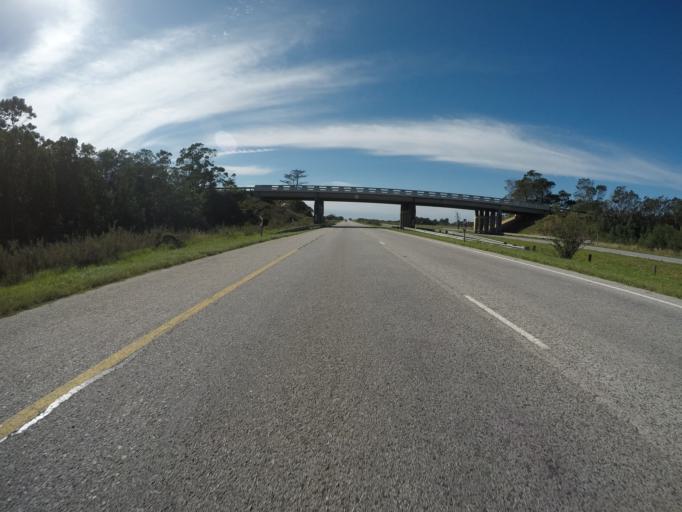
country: ZA
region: Eastern Cape
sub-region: Nelson Mandela Bay Metropolitan Municipality
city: Port Elizabeth
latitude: -33.9502
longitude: 25.4290
